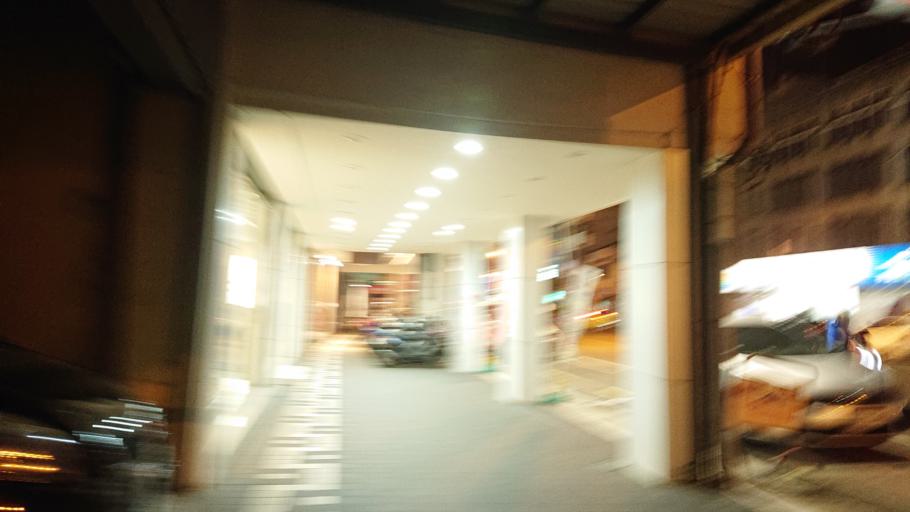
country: TW
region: Taiwan
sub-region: Tainan
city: Tainan
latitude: 22.9935
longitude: 120.2028
